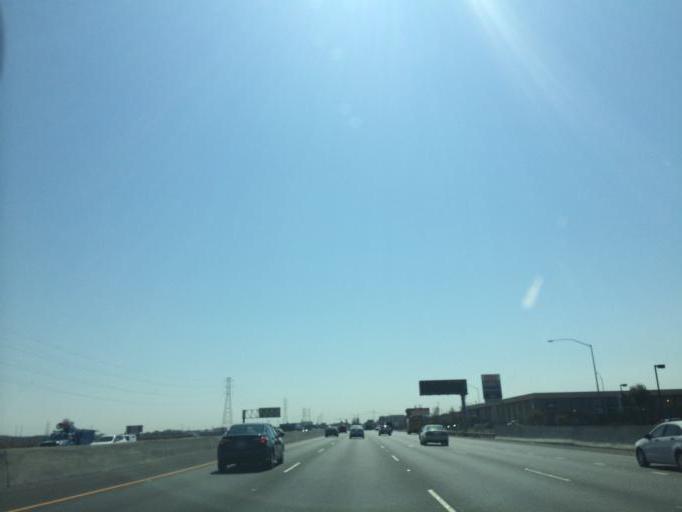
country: US
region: California
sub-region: San Mateo County
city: San Carlos
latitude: 37.5061
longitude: -122.2473
